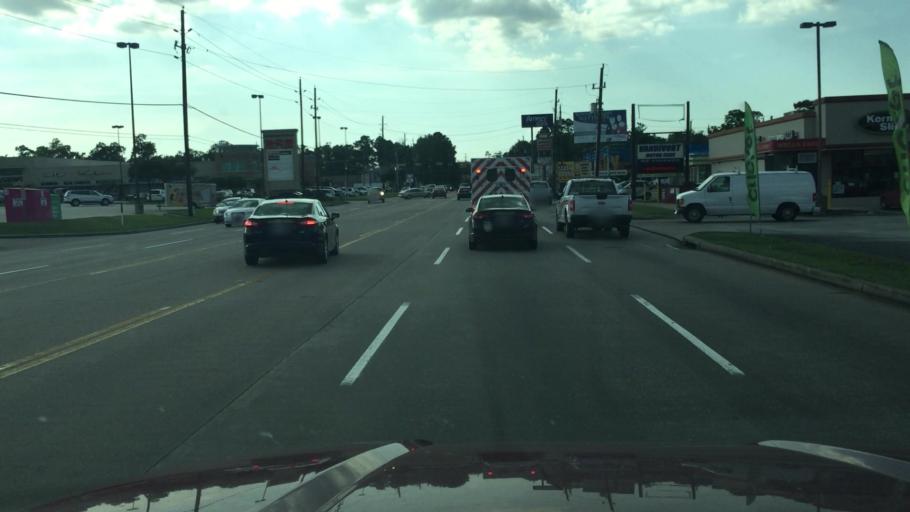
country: US
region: Texas
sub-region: Harris County
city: Tomball
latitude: 30.0220
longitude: -95.5249
